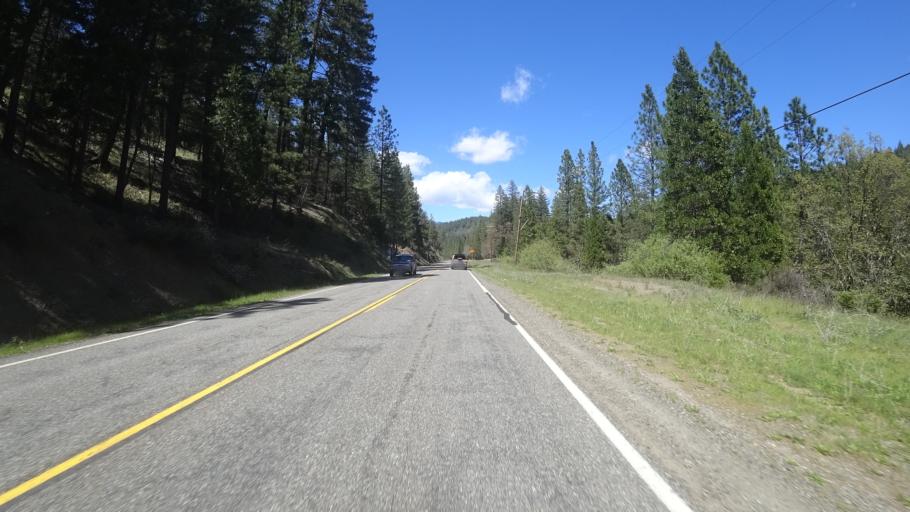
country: US
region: California
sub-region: Trinity County
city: Weaverville
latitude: 40.7520
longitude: -122.8869
